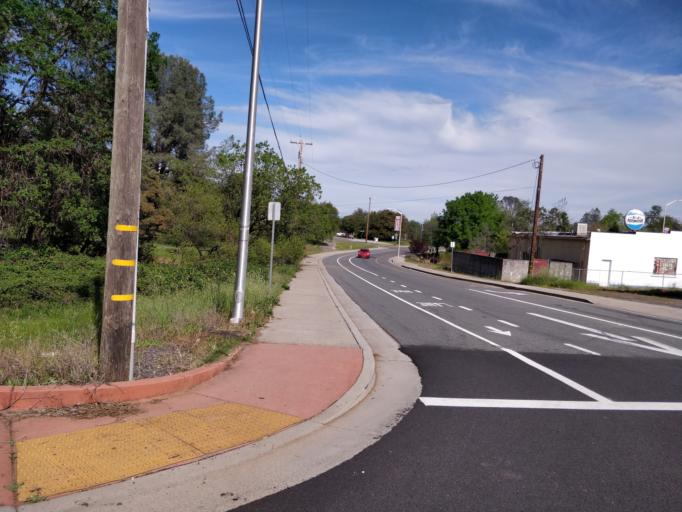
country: US
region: California
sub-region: Shasta County
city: Shasta Lake
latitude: 40.6811
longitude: -122.3690
